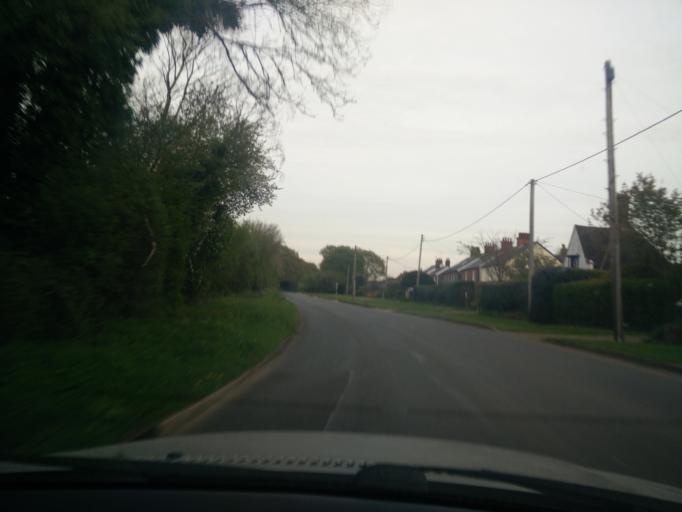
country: GB
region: England
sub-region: Buckinghamshire
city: Amersham
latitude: 51.6919
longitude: -0.6503
